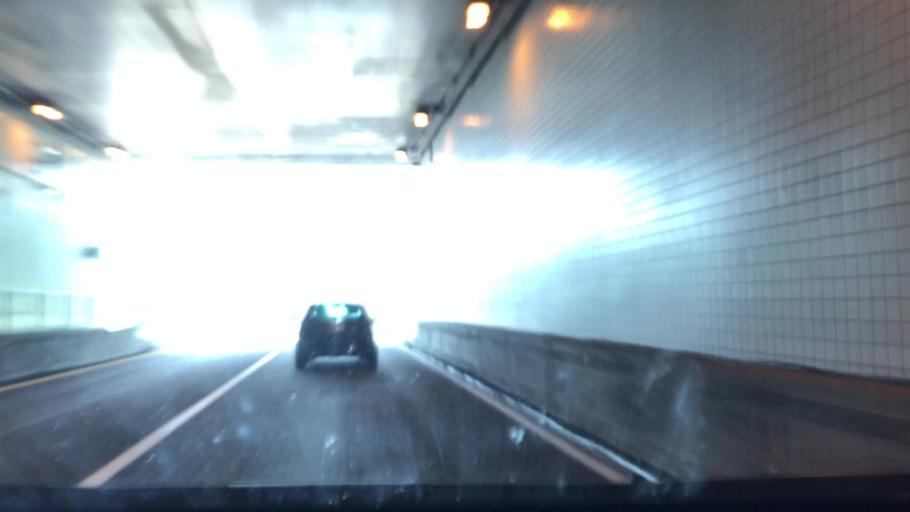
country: US
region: West Virginia
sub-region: Mercer County
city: Princeton
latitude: 37.2758
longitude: -81.1238
